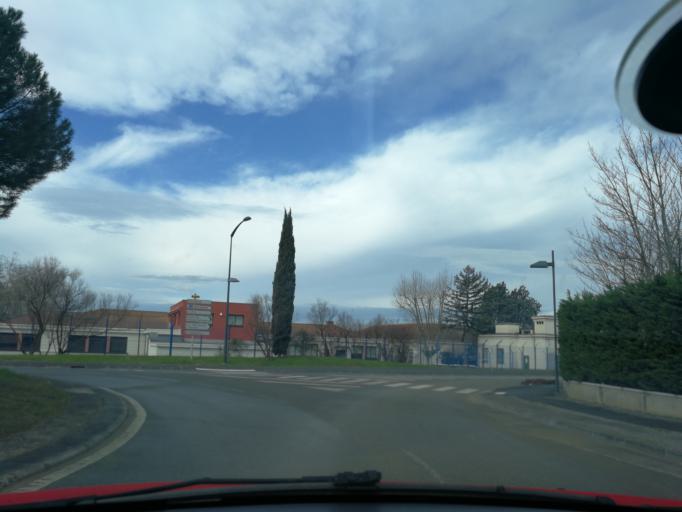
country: FR
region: Midi-Pyrenees
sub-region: Departement de la Haute-Garonne
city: Balma
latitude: 43.6222
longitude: 1.4888
